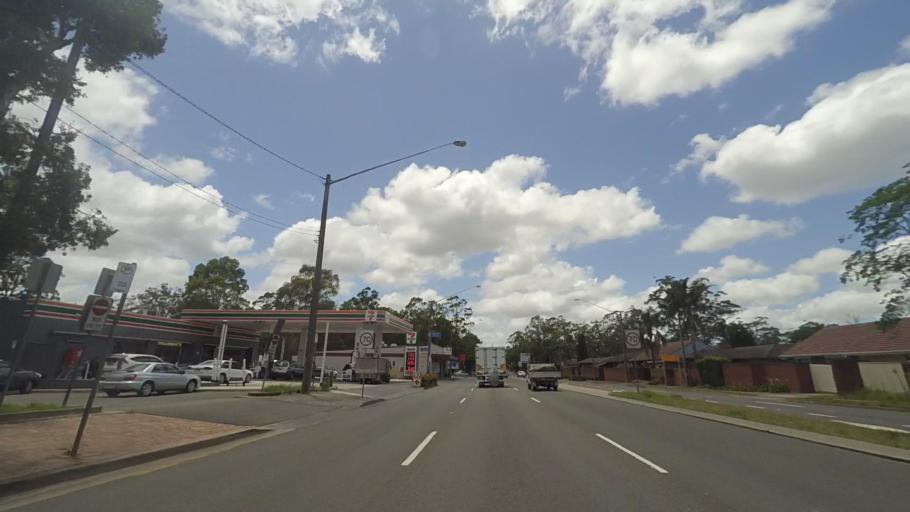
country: AU
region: New South Wales
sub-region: The Hills Shire
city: West Pennant
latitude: -33.7474
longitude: 151.0506
